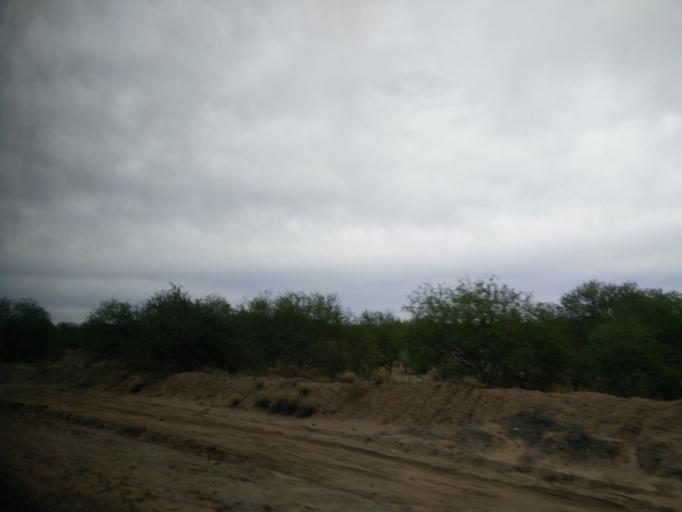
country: MX
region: Sonora
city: Hermosillo
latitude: 28.7454
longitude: -110.9741
